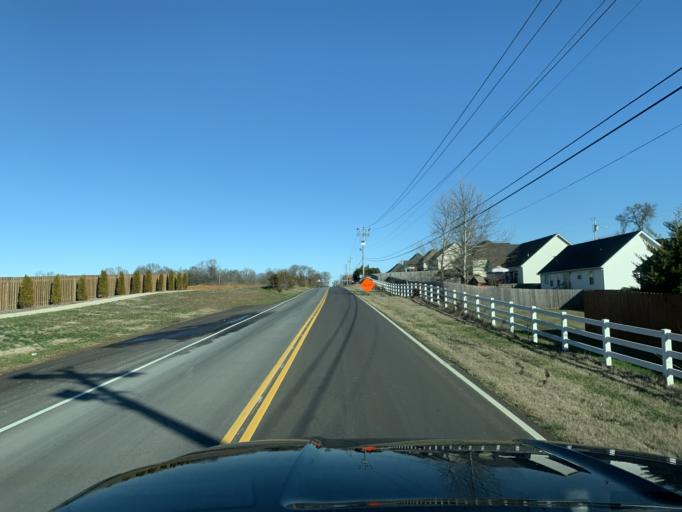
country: US
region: Tennessee
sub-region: Maury County
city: Spring Hill
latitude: 35.7497
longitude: -86.9026
